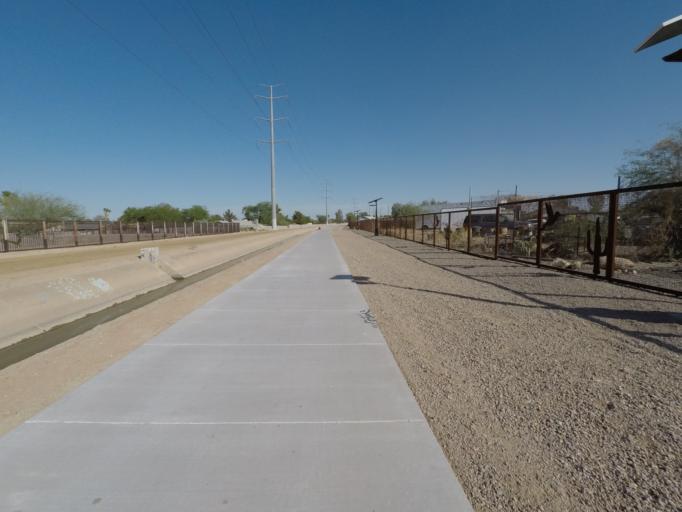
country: US
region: Arizona
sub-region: Maricopa County
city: Guadalupe
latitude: 33.3740
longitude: -111.9615
